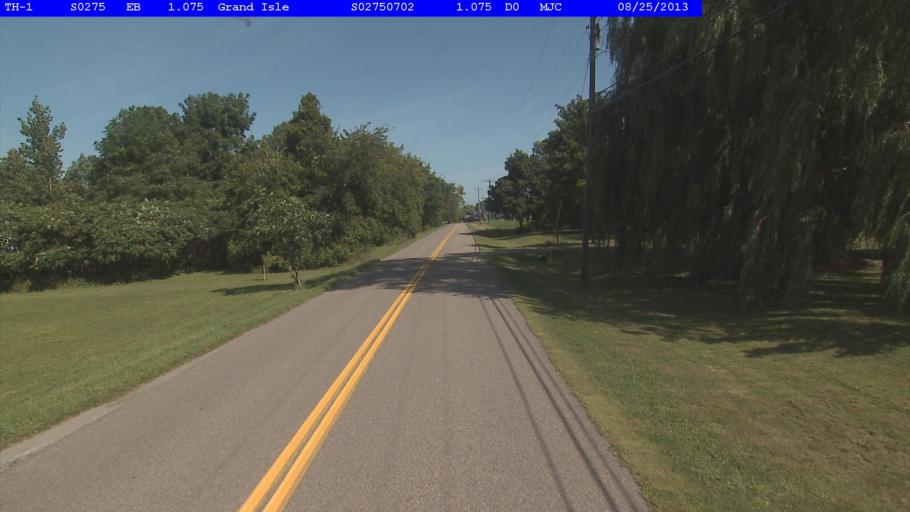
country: US
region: New York
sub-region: Clinton County
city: Cumberland Head
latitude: 44.7158
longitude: -73.3417
